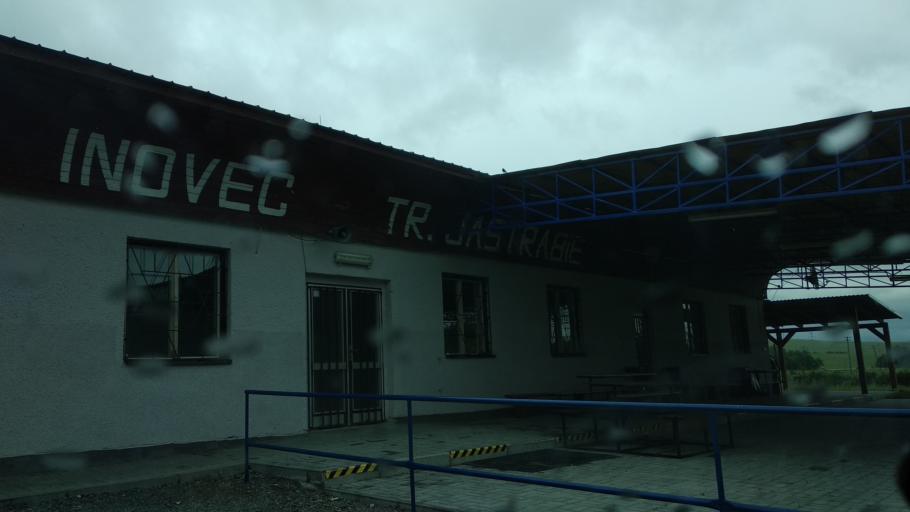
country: SK
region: Nitriansky
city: Trencianske Teplice
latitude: 48.8027
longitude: 18.1191
